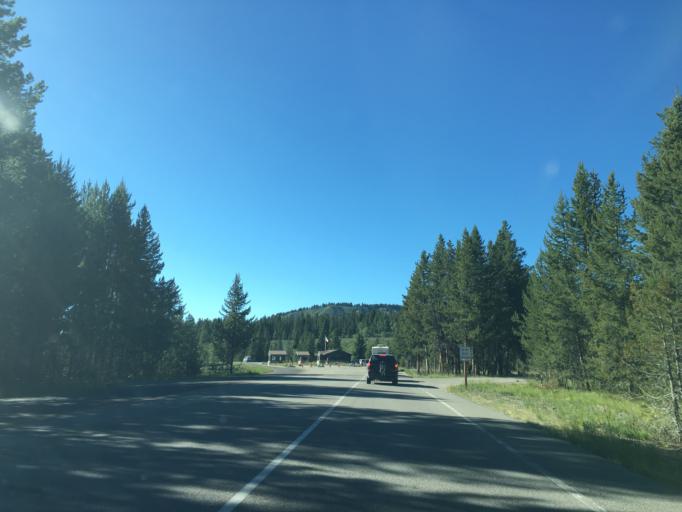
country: US
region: Wyoming
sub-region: Teton County
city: Jackson
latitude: 43.8425
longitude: -110.5112
